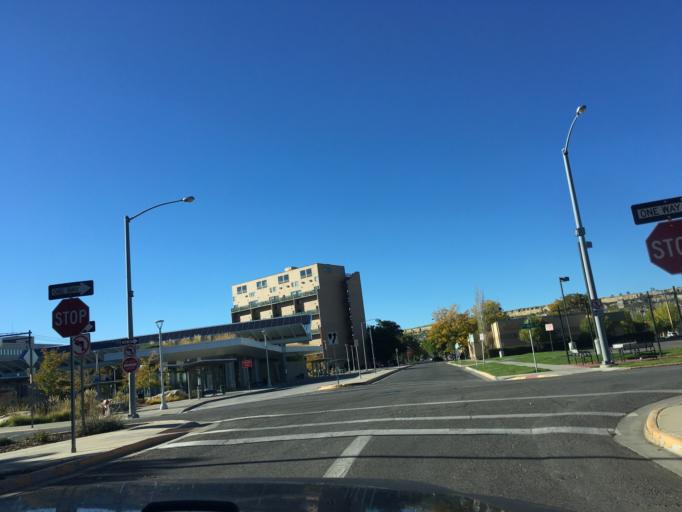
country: US
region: Montana
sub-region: Yellowstone County
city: Billings
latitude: 45.7846
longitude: -108.5028
